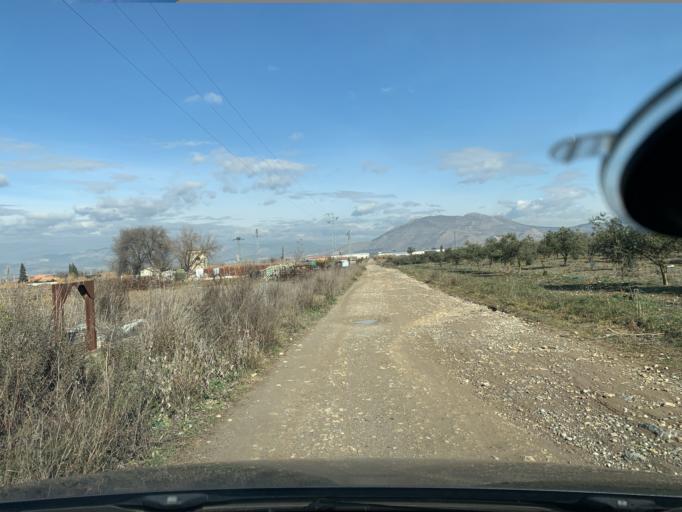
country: ES
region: Andalusia
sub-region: Provincia de Granada
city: Chauchina
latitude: 37.1803
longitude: -3.7507
